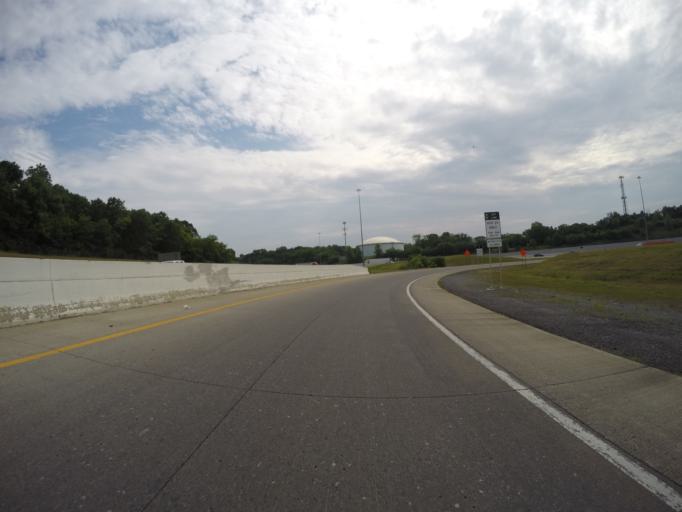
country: US
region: Tennessee
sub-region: Davidson County
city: Goodlettsville
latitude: 36.2665
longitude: -86.7391
